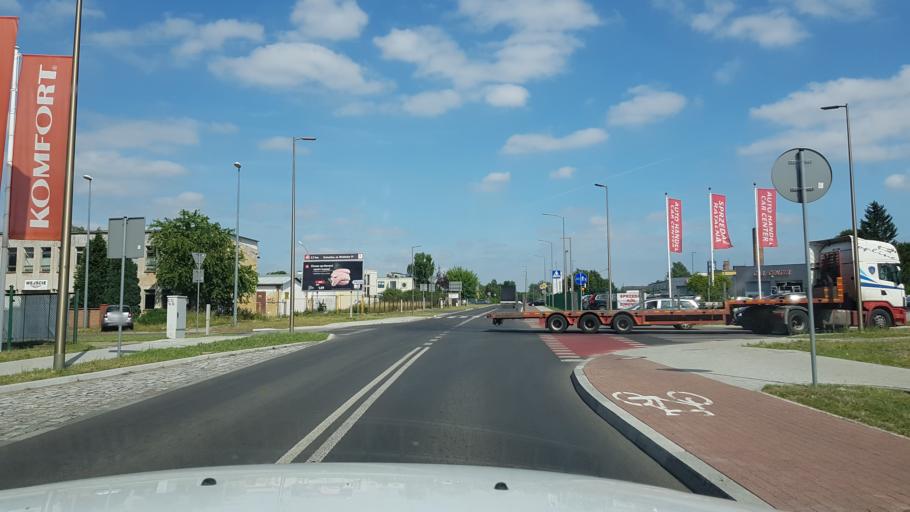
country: PL
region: West Pomeranian Voivodeship
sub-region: Powiat goleniowski
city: Goleniow
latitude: 53.5612
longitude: 14.8455
